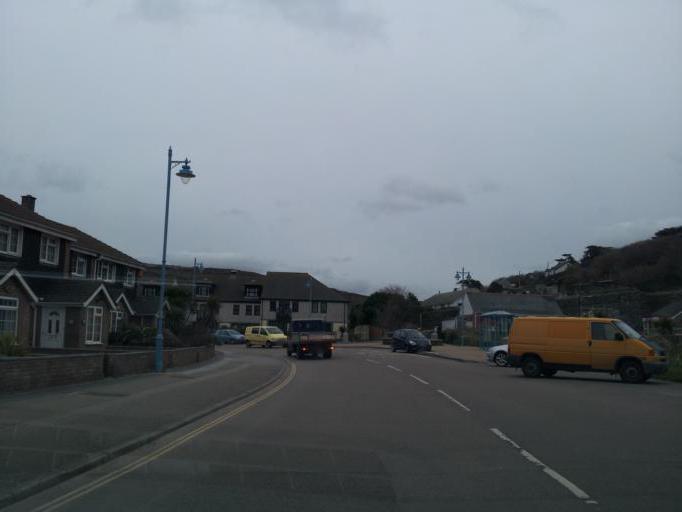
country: GB
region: England
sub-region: Cornwall
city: Camborne
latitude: 50.2605
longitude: -5.2898
